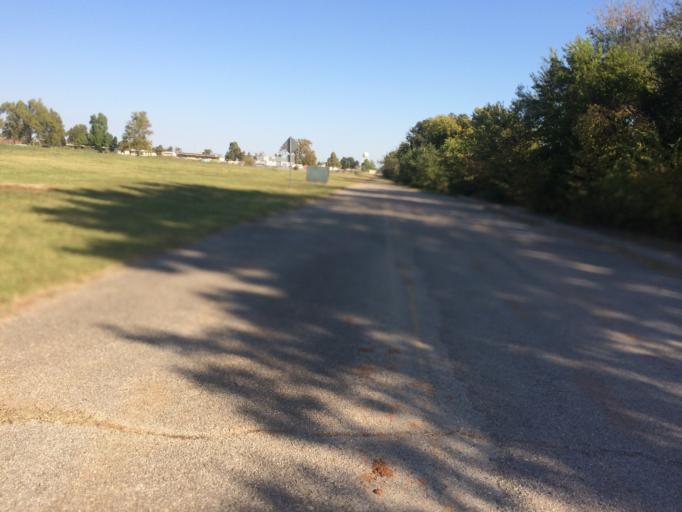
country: US
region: Oklahoma
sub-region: Cleveland County
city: Norman
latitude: 35.1811
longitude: -97.4322
